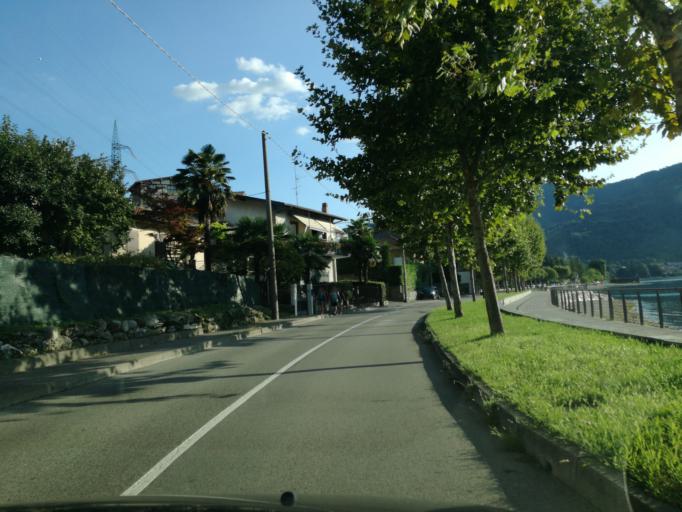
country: IT
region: Lombardy
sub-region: Provincia di Lecco
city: Vercurago
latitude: 45.8117
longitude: 9.4206
